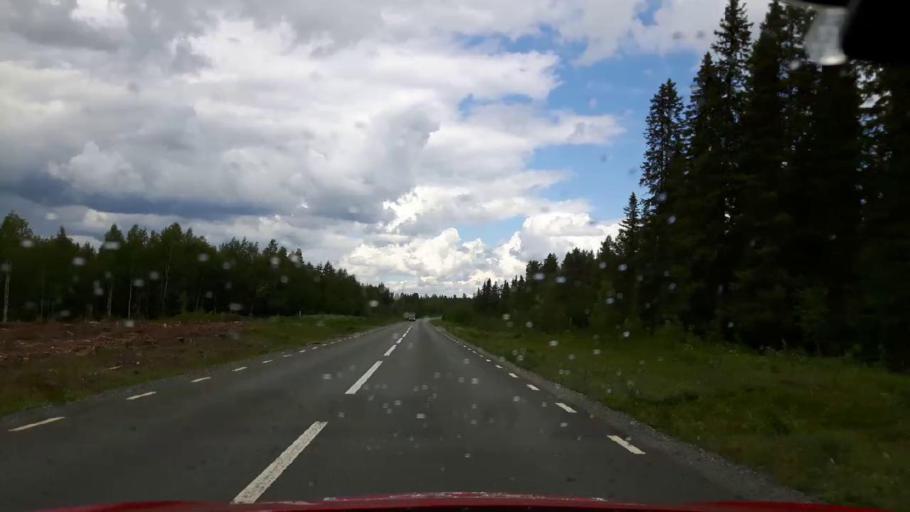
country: SE
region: Jaemtland
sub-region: Krokoms Kommun
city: Krokom
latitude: 63.5842
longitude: 14.2931
